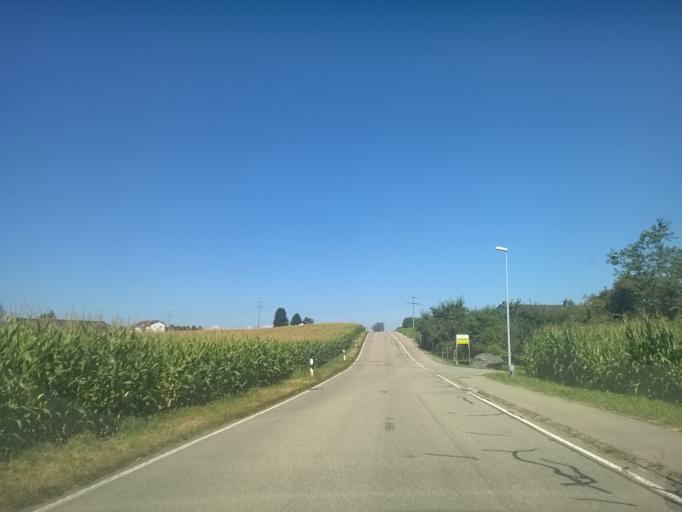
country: CH
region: Zurich
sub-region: Bezirk Winterthur
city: Brutten
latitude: 47.4742
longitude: 8.6670
